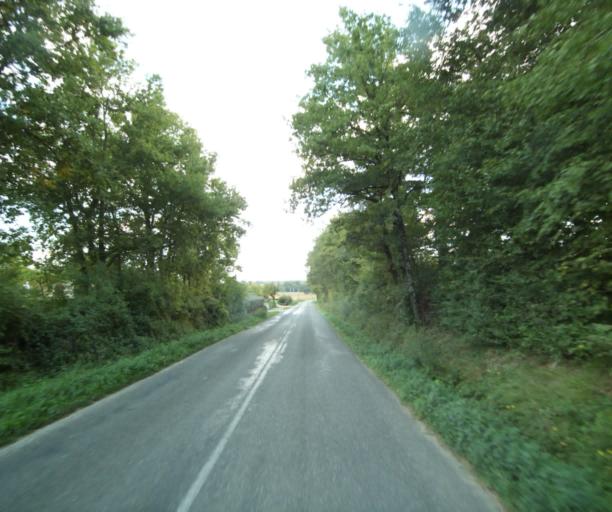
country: FR
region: Midi-Pyrenees
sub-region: Departement du Gers
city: Cazaubon
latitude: 43.9182
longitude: -0.0790
